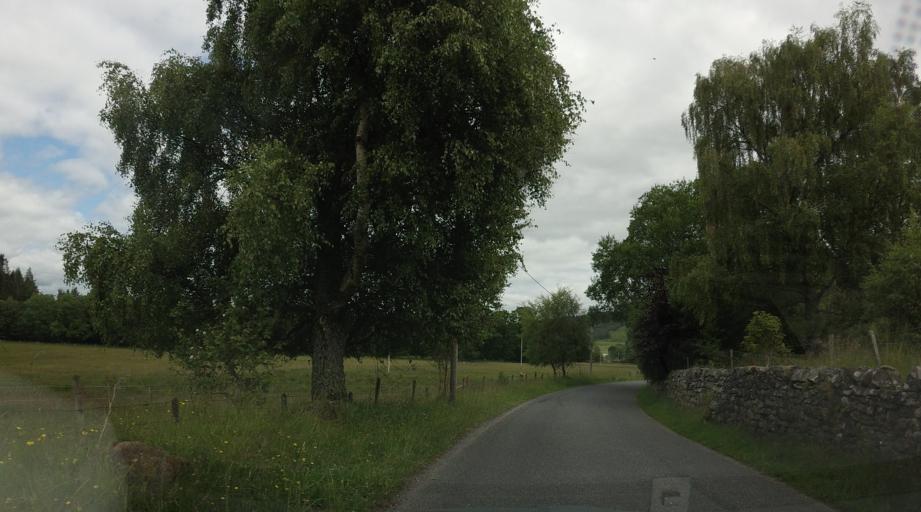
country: GB
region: Scotland
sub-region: Perth and Kinross
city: Aberfeldy
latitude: 56.6922
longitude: -4.1575
